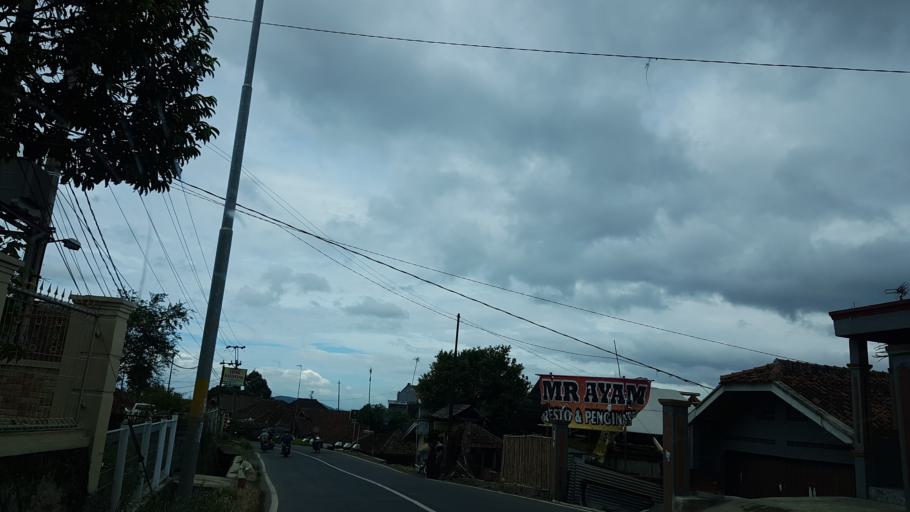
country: ID
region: West Java
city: Banjar
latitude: -7.1187
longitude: 107.4340
